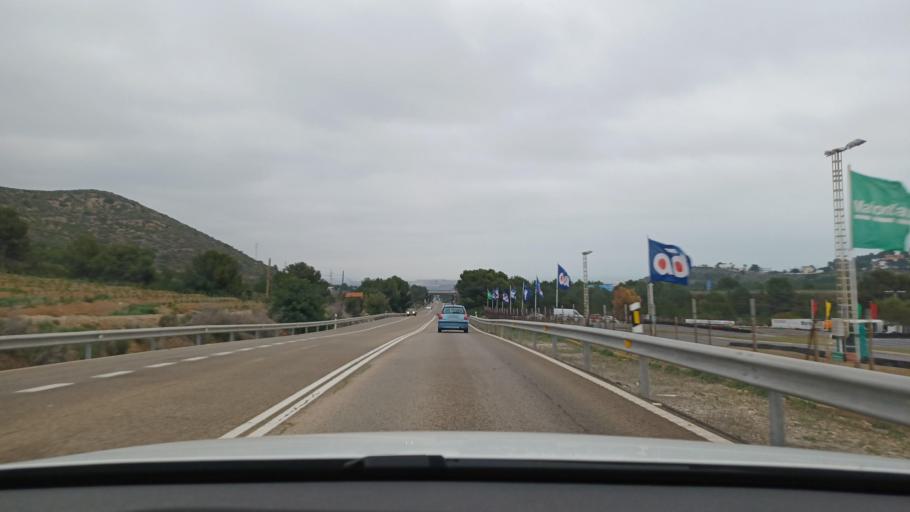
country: ES
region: Valencia
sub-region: Provincia de Castello
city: Orpesa/Oropesa del Mar
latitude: 40.0785
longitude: 0.1146
